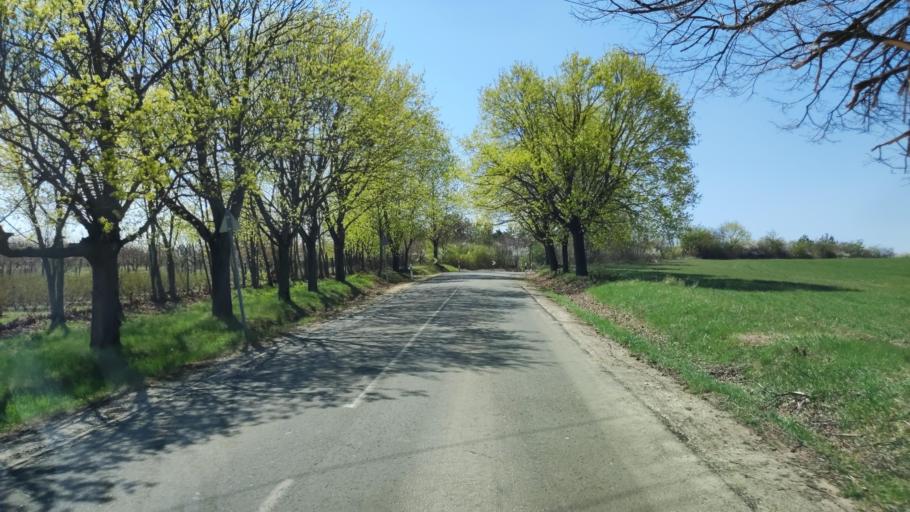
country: HU
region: Pest
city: Kosd
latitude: 47.7937
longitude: 19.1764
